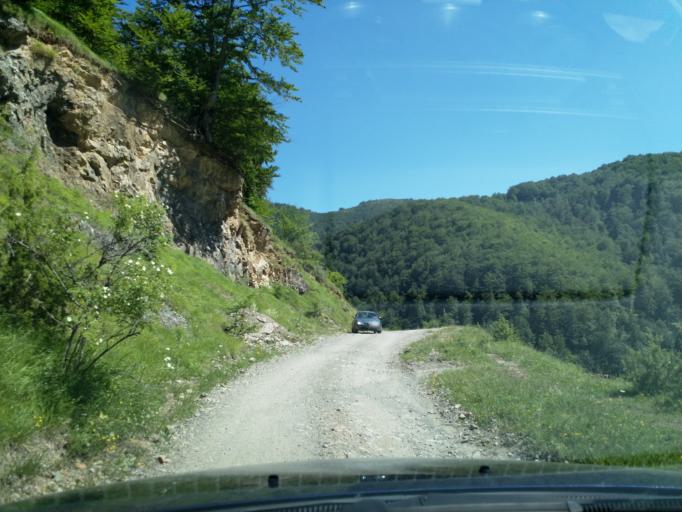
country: XK
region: Mitrovica
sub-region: Komuna e Leposaviqit
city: Leposaviq
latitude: 43.2662
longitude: 20.8606
